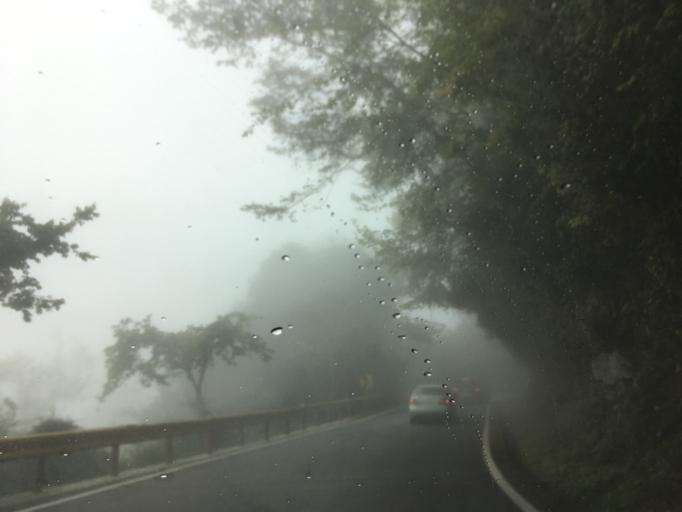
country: TW
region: Taiwan
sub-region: Hualien
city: Hualian
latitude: 24.1847
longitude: 121.4206
